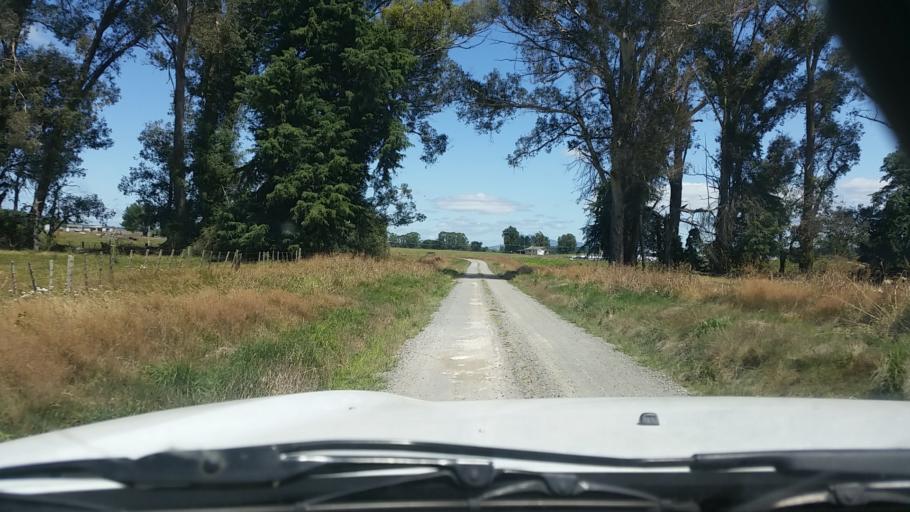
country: NZ
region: Waikato
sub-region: Taupo District
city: Taupo
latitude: -38.5208
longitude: 176.3672
